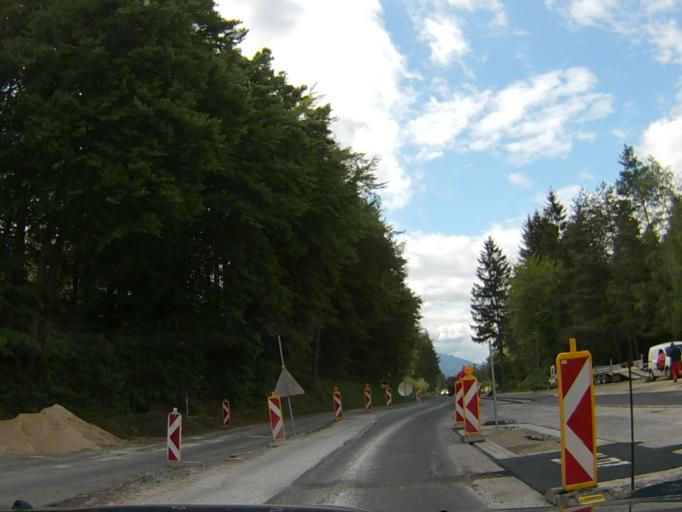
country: AT
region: Carinthia
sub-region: Politischer Bezirk Villach Land
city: Fresach
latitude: 46.6649
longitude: 13.7312
